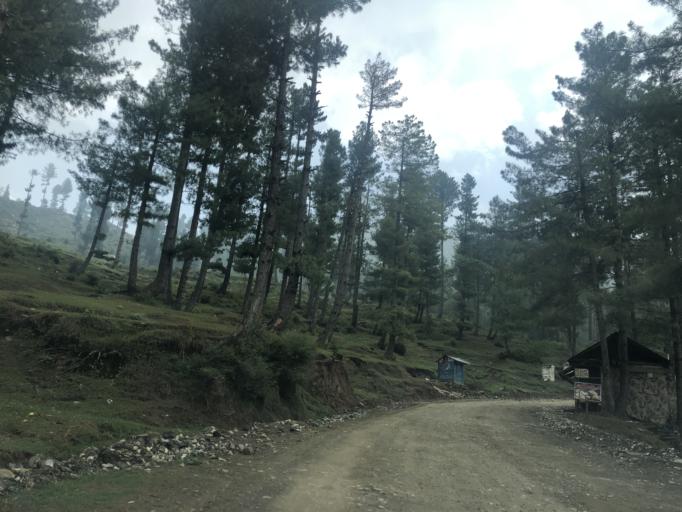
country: PK
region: Khyber Pakhtunkhwa
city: Alpurai
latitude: 34.8170
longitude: 72.5742
